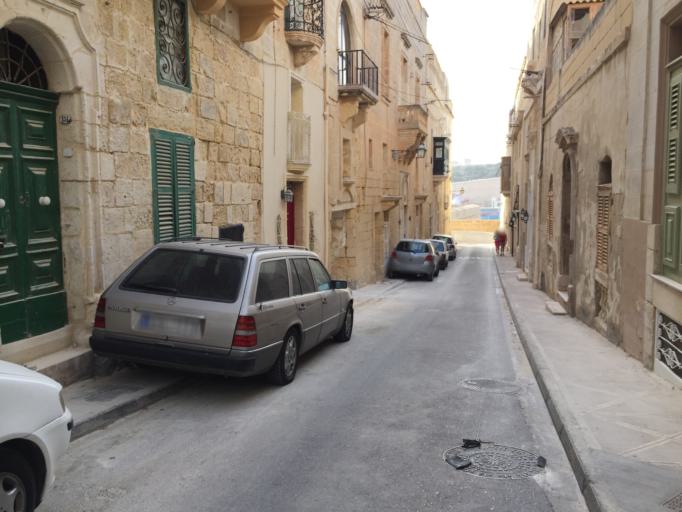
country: MT
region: L-Isla
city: Senglea
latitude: 35.8900
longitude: 14.5152
